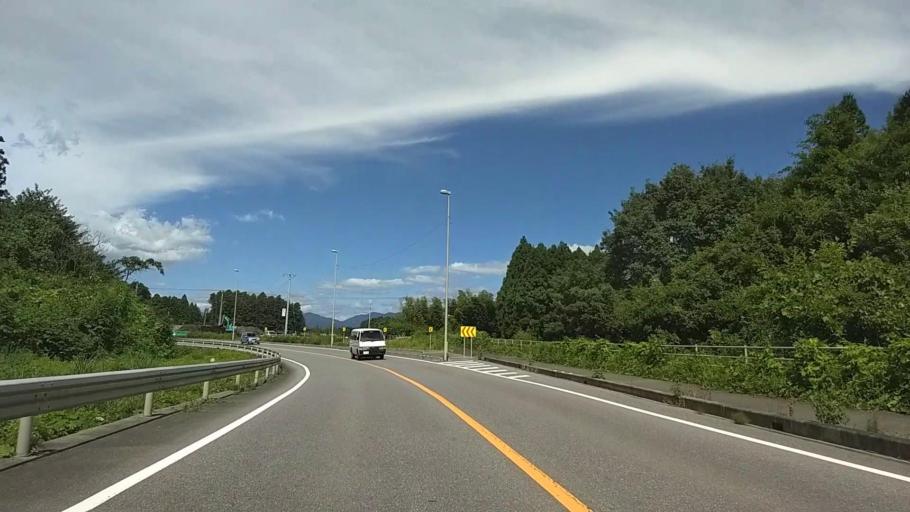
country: JP
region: Tochigi
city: Imaichi
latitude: 36.7056
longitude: 139.7486
